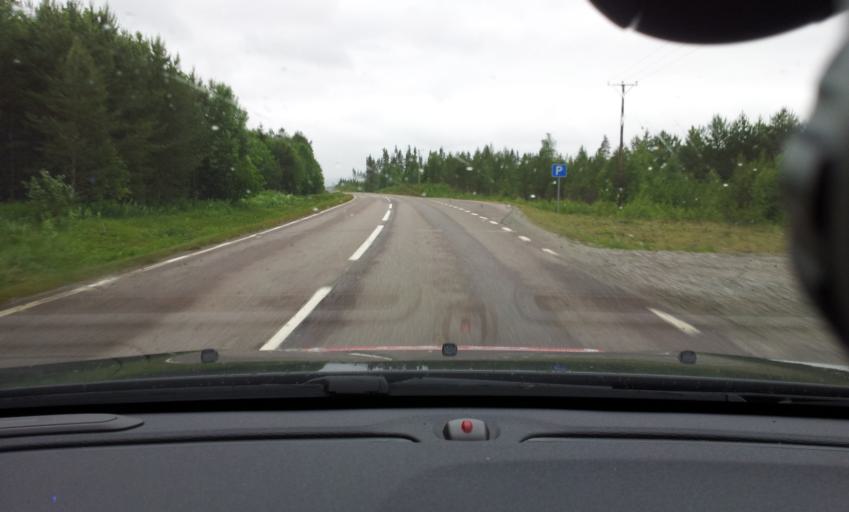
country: SE
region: Jaemtland
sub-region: Ragunda Kommun
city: Hammarstrand
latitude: 63.2054
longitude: 15.9468
